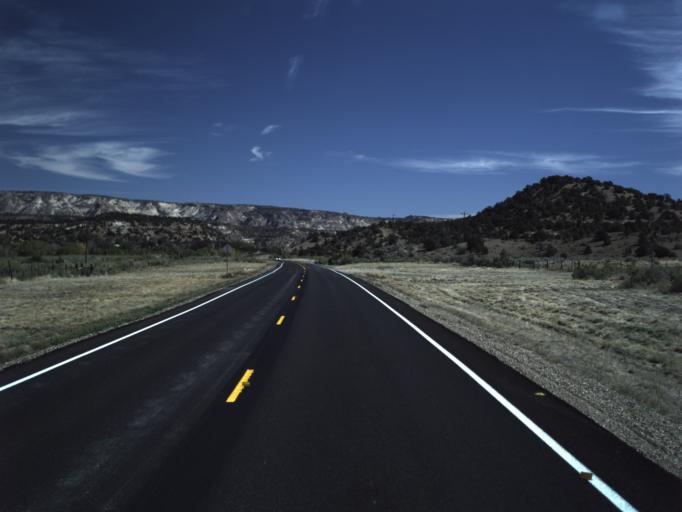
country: US
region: Utah
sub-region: Wayne County
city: Loa
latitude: 37.7690
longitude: -111.6668
